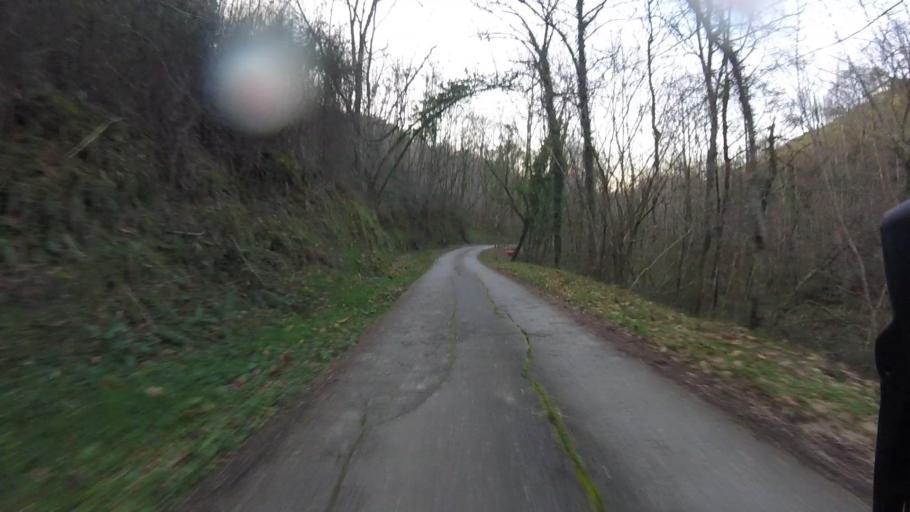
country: ES
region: Basque Country
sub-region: Provincia de Guipuzcoa
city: Errenteria
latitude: 43.2746
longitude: -1.8670
